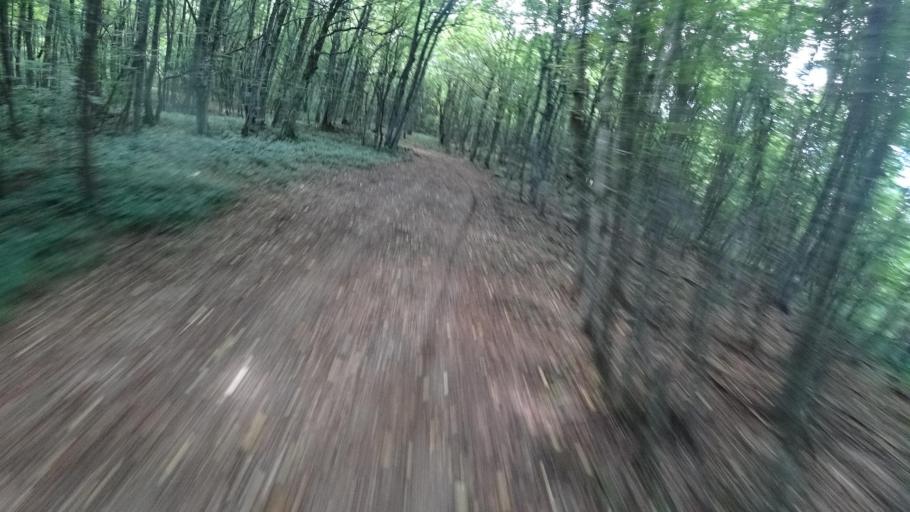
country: HR
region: Karlovacka
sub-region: Grad Ogulin
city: Ogulin
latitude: 45.2533
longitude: 15.1911
